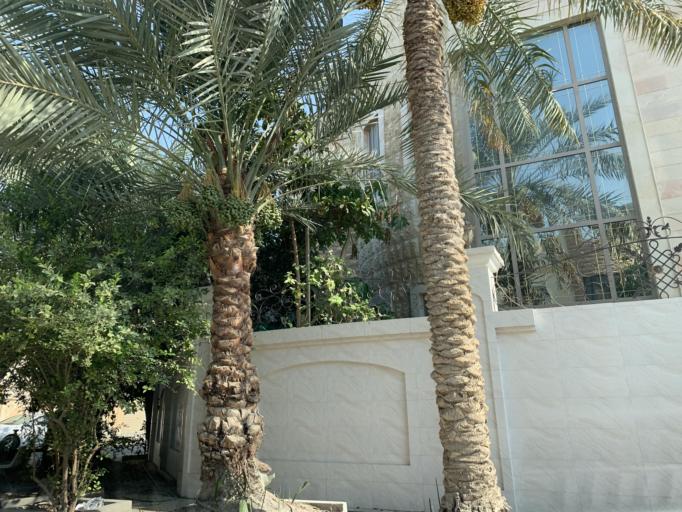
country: BH
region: Manama
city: Jidd Hafs
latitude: 26.1973
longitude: 50.5171
